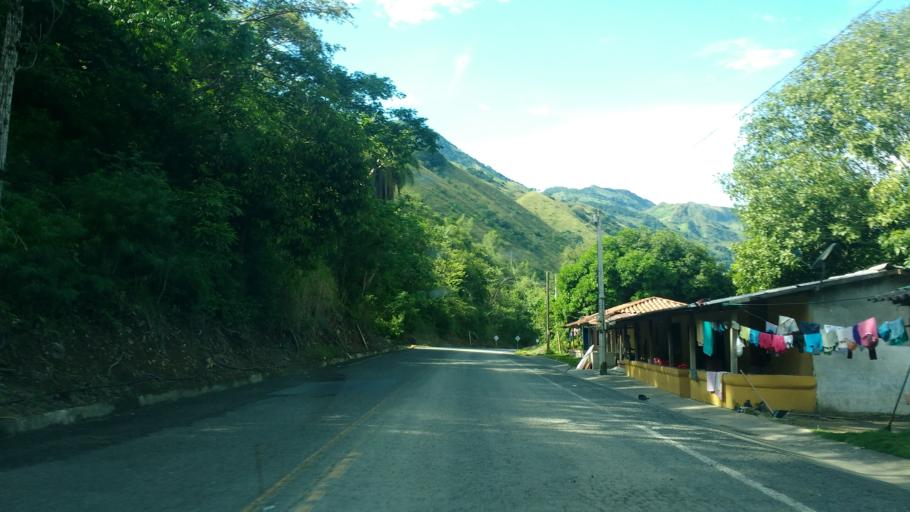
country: CO
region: Antioquia
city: Concordia
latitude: 6.0417
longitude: -75.8627
